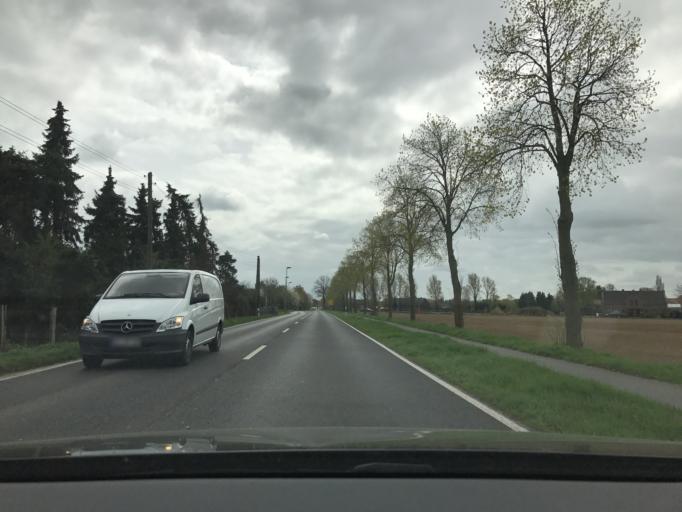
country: DE
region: North Rhine-Westphalia
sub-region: Regierungsbezirk Dusseldorf
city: Kaarst
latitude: 51.2824
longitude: 6.6111
